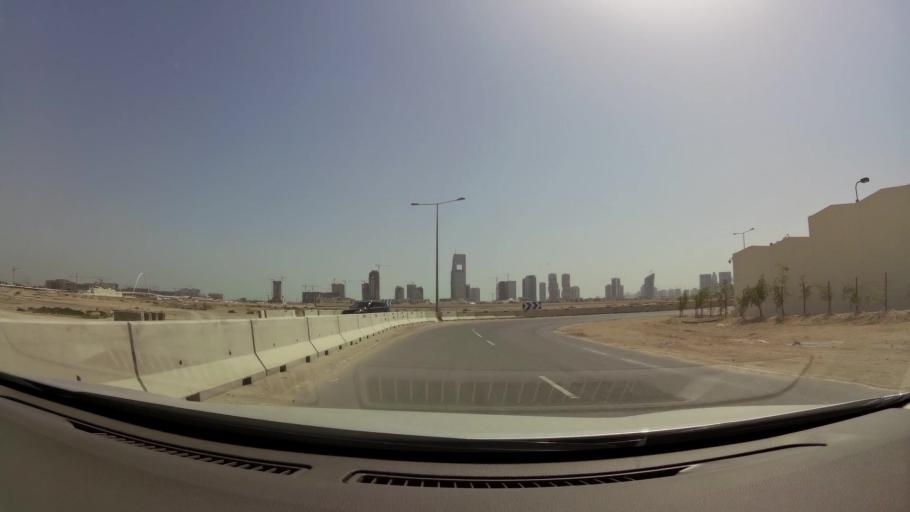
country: QA
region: Baladiyat Umm Salal
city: Umm Salal Muhammad
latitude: 25.3922
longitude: 51.5031
